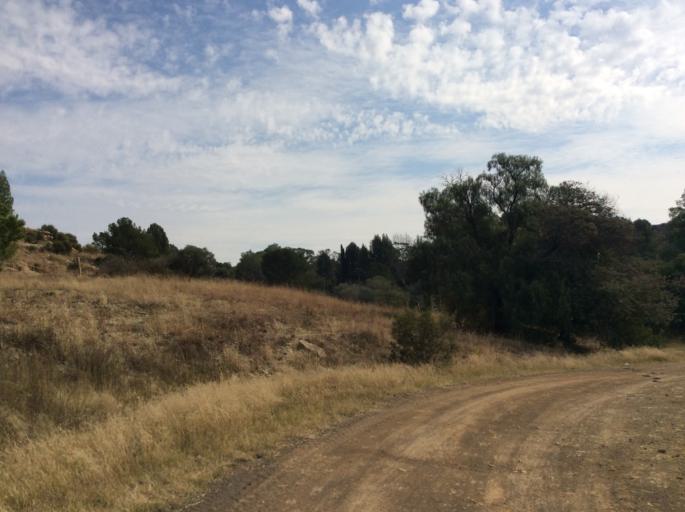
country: ZA
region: Orange Free State
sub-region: Xhariep District Municipality
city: Dewetsdorp
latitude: -29.5889
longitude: 26.6616
